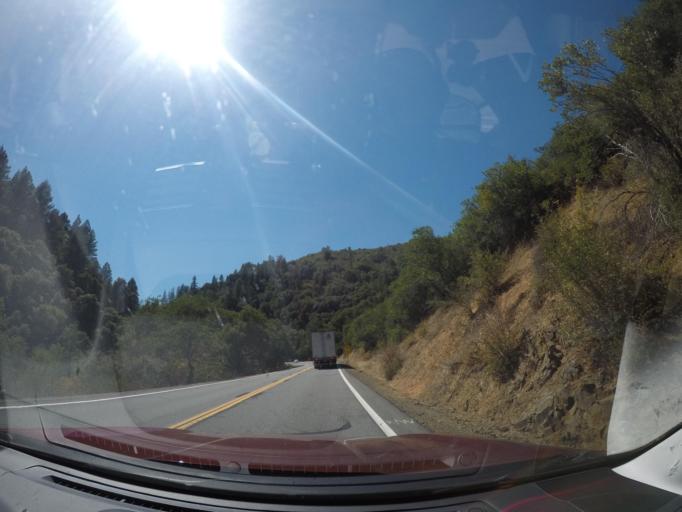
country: US
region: California
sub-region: Shasta County
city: Bella Vista
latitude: 40.7464
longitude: -122.0593
